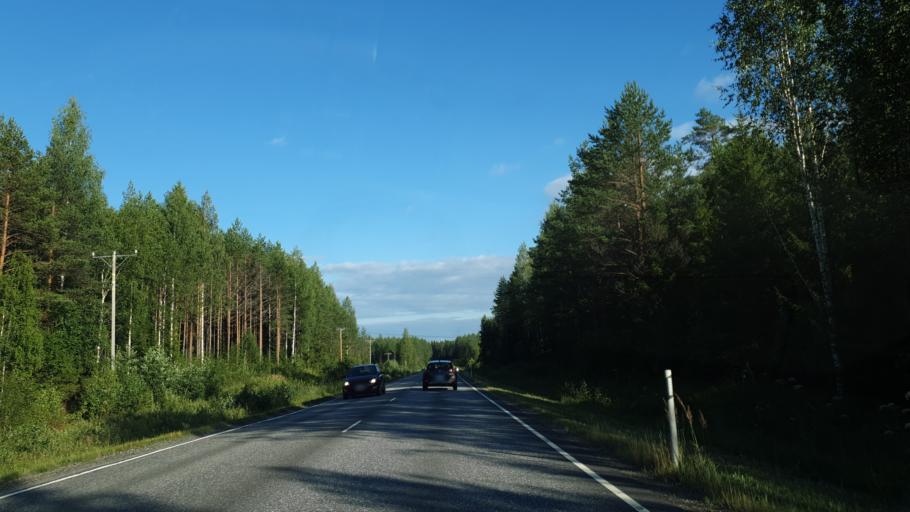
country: FI
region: North Karelia
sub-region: Joensuu
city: Outokumpu
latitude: 62.5277
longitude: 28.9913
